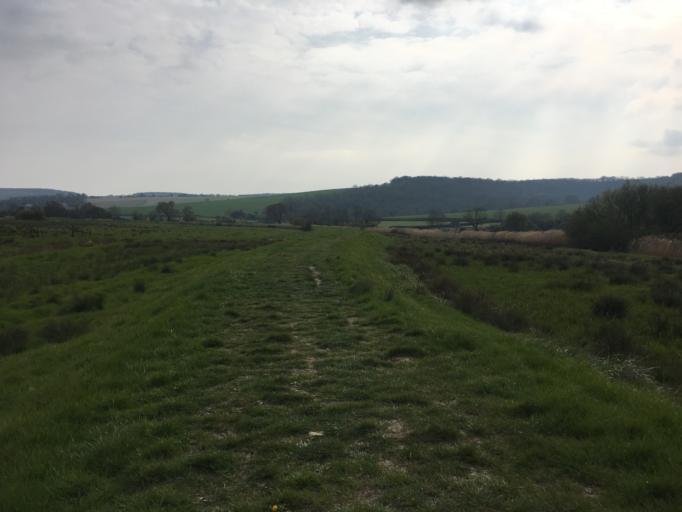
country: GB
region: England
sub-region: West Sussex
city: Arundel
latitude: 50.9072
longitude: -0.5534
